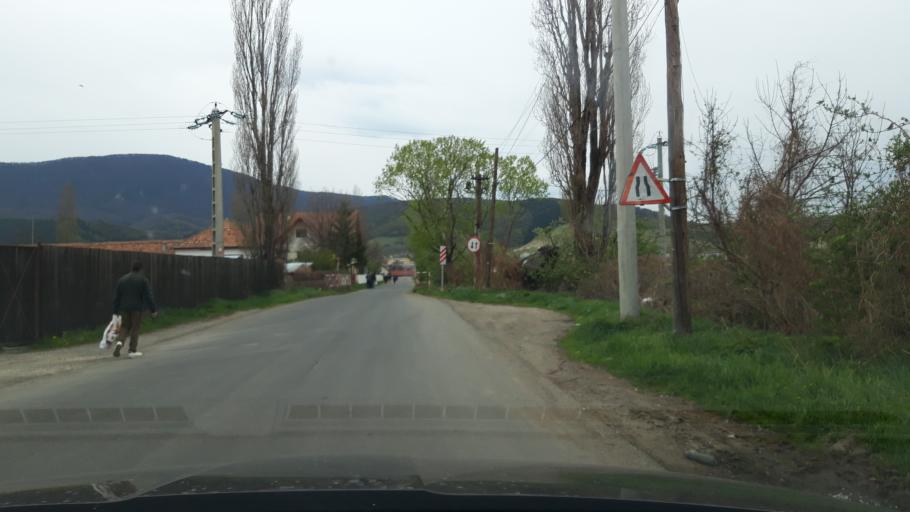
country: RO
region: Brasov
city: Codlea
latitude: 45.6998
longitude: 25.4594
